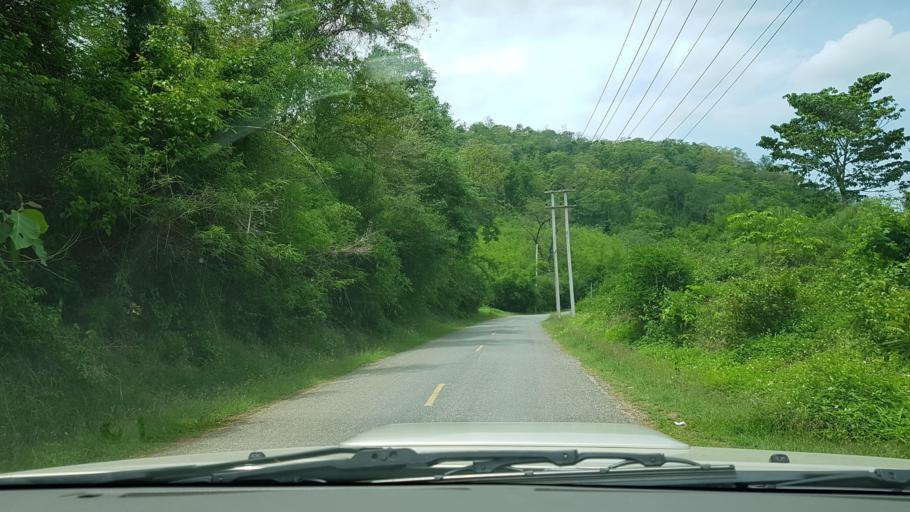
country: TH
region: Nan
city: Chaloem Phra Kiat
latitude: 19.9588
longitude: 101.2565
